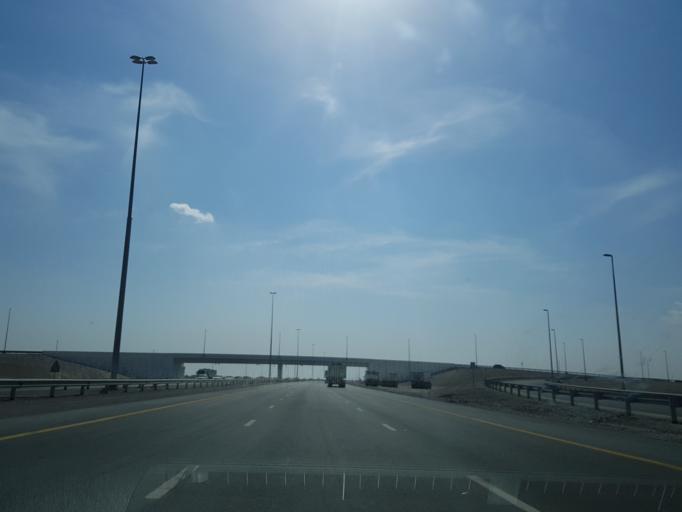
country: AE
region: Ra's al Khaymah
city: Ras al-Khaimah
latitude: 25.7187
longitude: 56.0081
